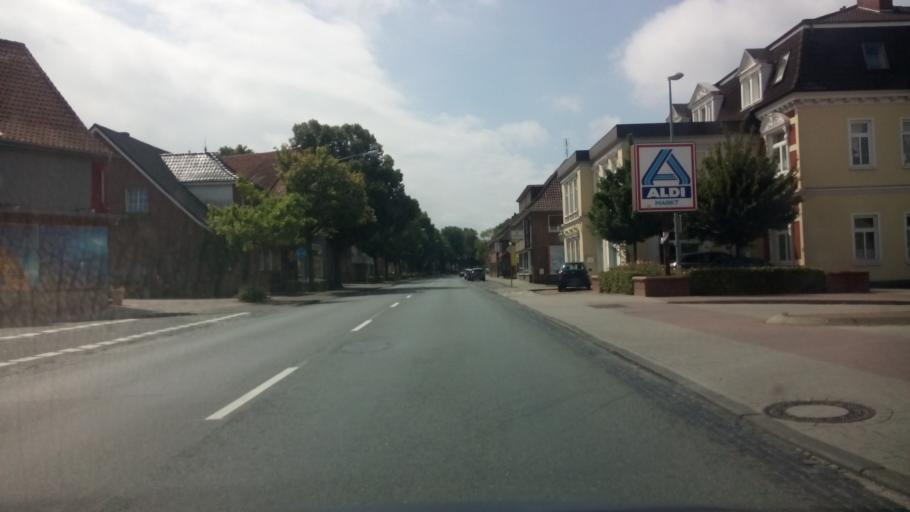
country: DE
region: Lower Saxony
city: Twistringen
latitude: 52.7993
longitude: 8.6382
